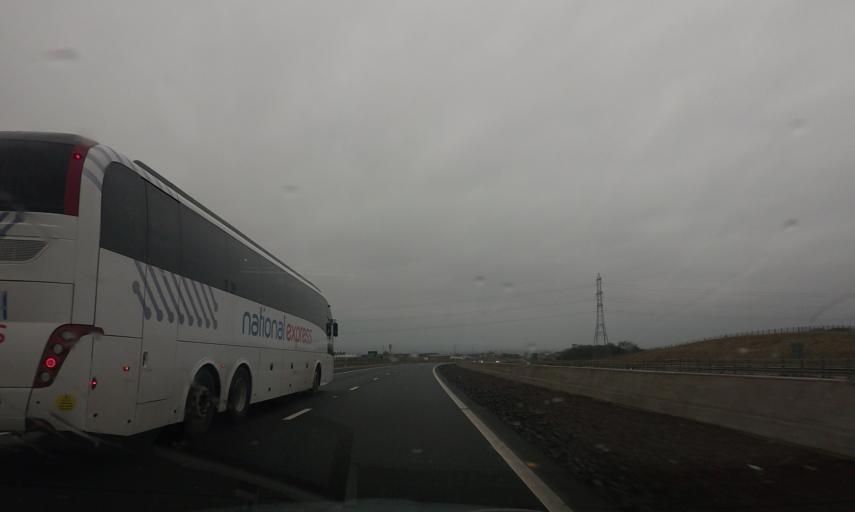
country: GB
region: Scotland
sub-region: North Lanarkshire
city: Chapelhall
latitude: 55.8330
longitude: -3.9379
